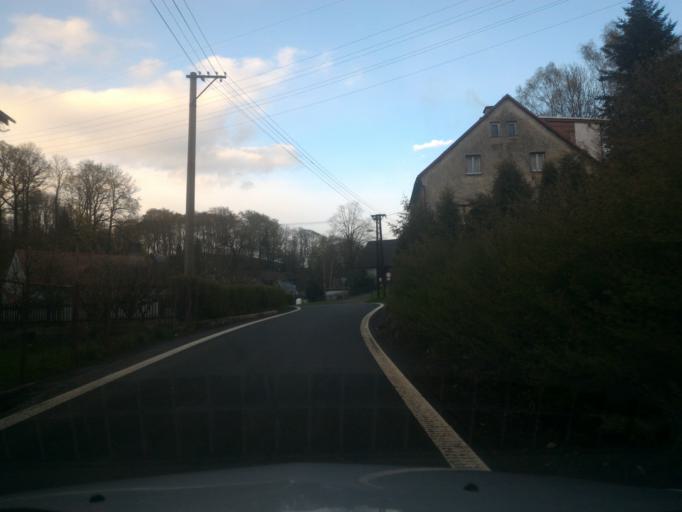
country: CZ
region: Ustecky
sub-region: Okres Decin
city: Krasna Lipa
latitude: 50.9152
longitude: 14.5209
